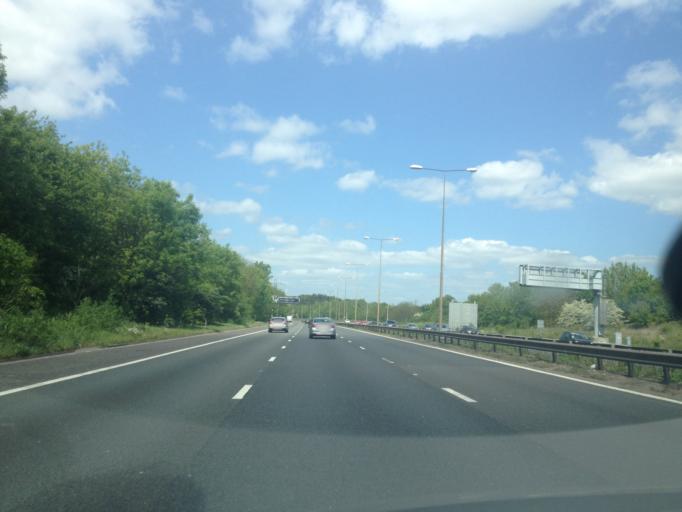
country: GB
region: England
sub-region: Hertfordshire
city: Bushey
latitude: 51.6538
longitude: -0.3438
